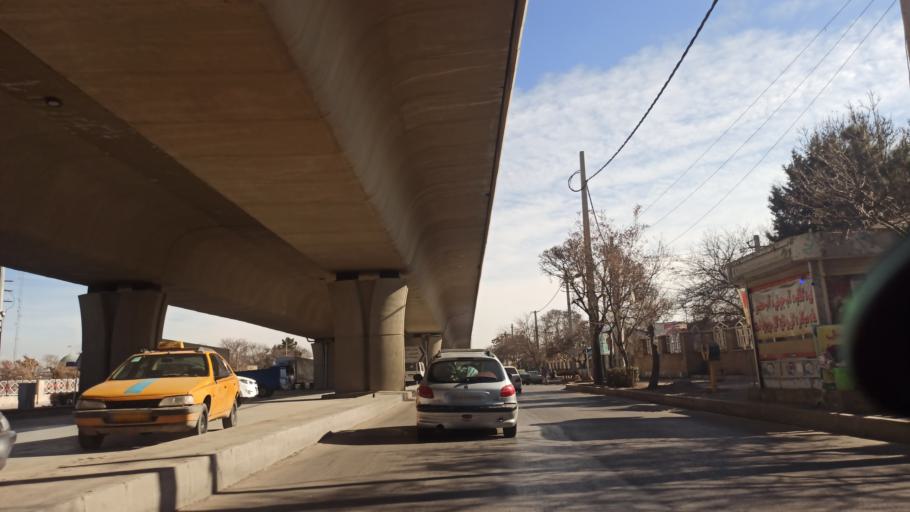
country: IR
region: Qazvin
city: Qazvin
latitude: 36.2569
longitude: 49.9951
